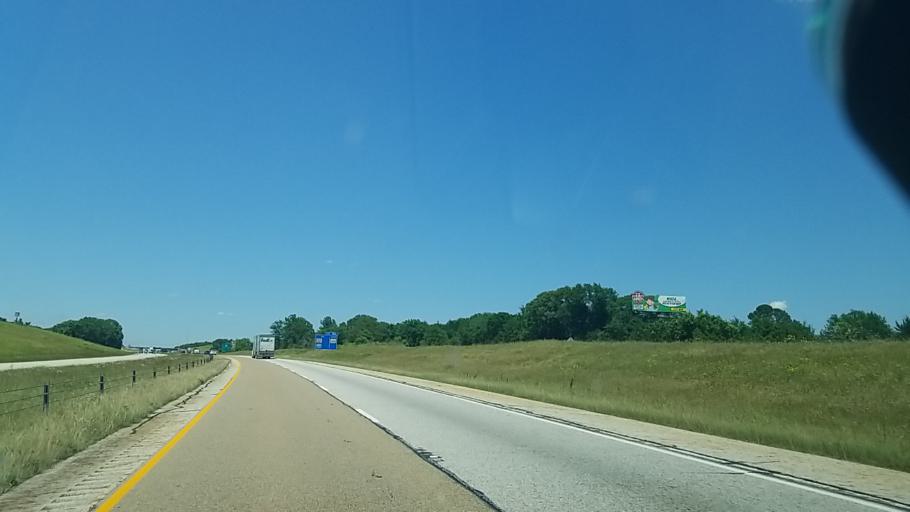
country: US
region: Texas
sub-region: Leon County
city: Centerville
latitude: 31.2478
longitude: -95.9891
